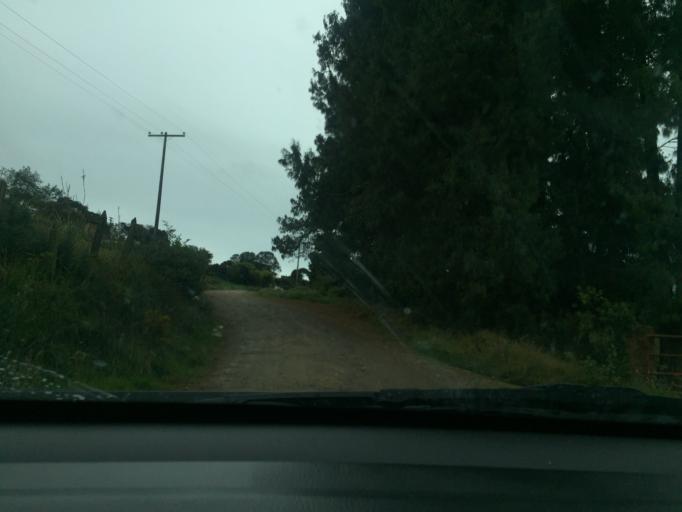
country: CO
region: Cundinamarca
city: El Rosal
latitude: 4.8685
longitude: -74.2940
